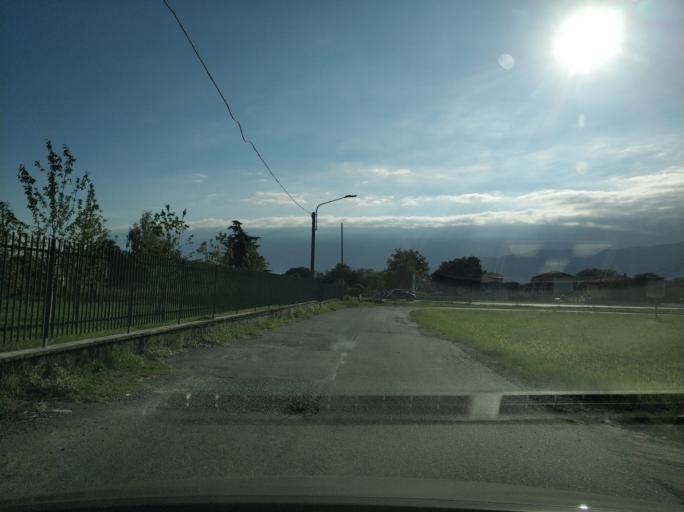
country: IT
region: Piedmont
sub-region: Provincia di Torino
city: Cirie
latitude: 45.2349
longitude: 7.5873
